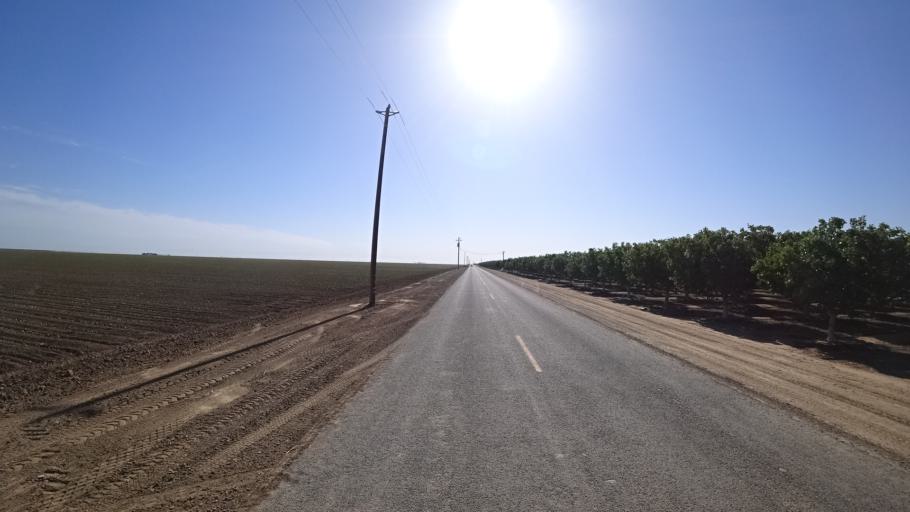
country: US
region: California
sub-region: Kings County
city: Kettleman City
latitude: 36.1088
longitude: -120.0181
